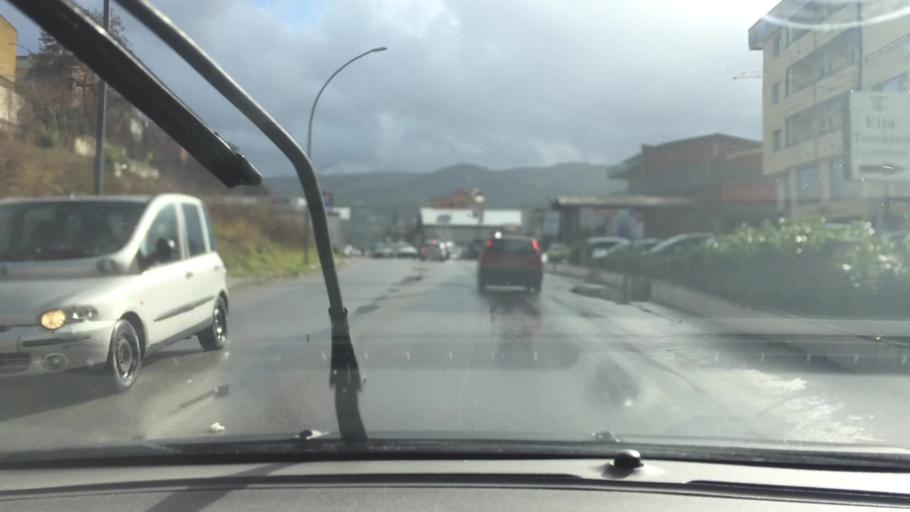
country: IT
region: Basilicate
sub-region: Provincia di Potenza
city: Potenza
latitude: 40.6322
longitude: 15.7887
